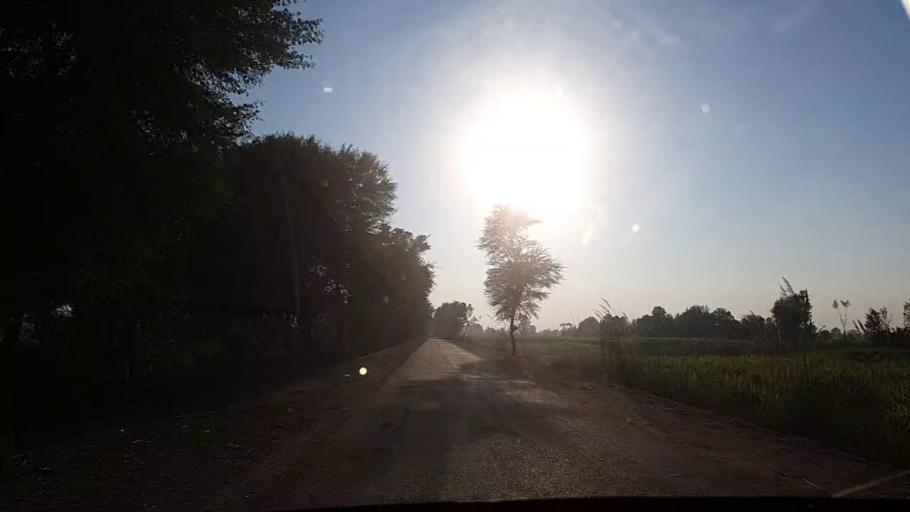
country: PK
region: Sindh
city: Sobhadero
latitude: 27.4166
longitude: 68.4015
